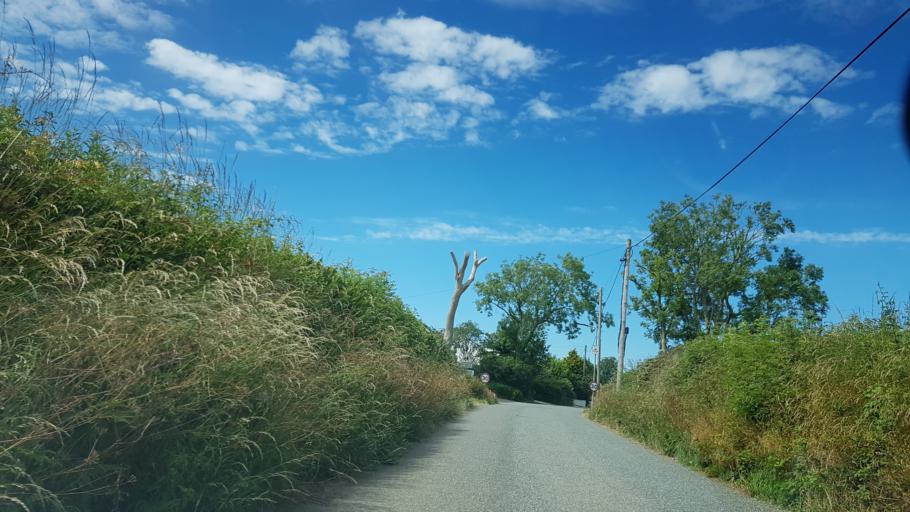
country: GB
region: Wales
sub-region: Pembrokeshire
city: Haverfordwest
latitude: 51.8221
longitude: -4.9448
